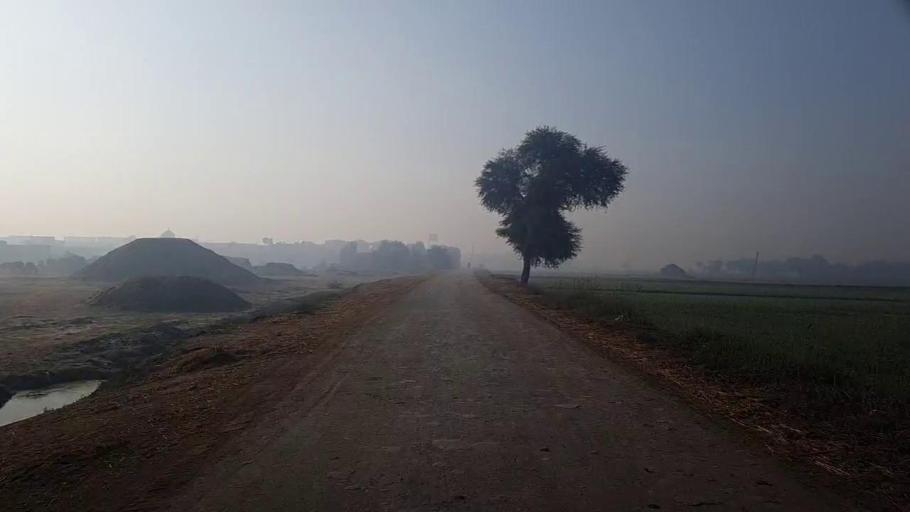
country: PK
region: Sindh
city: Mehar
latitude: 27.1385
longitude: 67.8233
